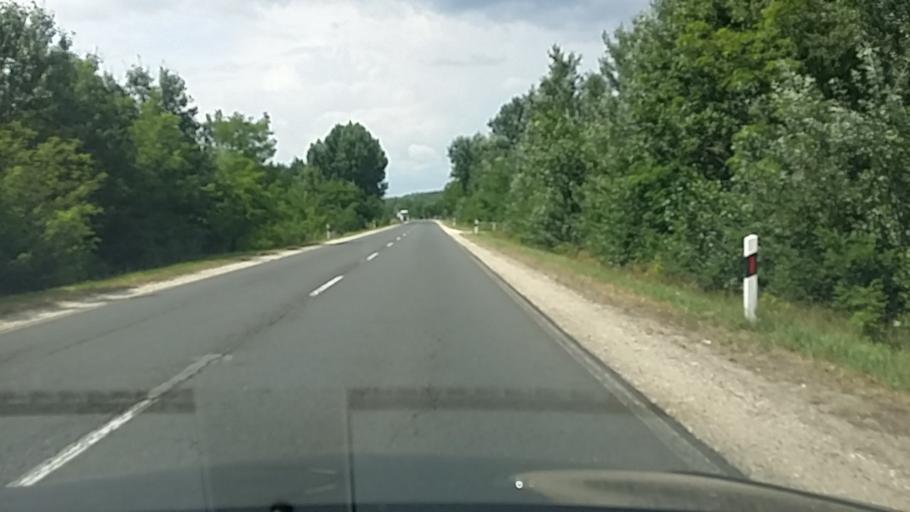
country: HU
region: Pest
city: Taborfalva
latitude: 47.0823
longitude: 19.4873
